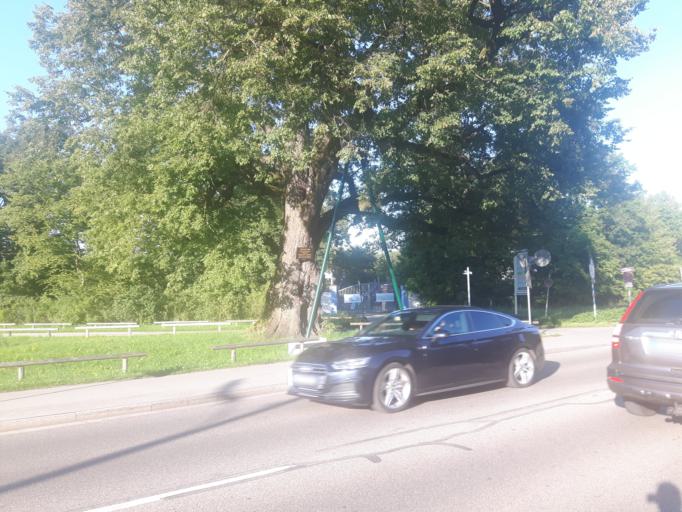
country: DE
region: Bavaria
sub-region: Upper Bavaria
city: Pasing
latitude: 48.1680
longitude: 11.5151
